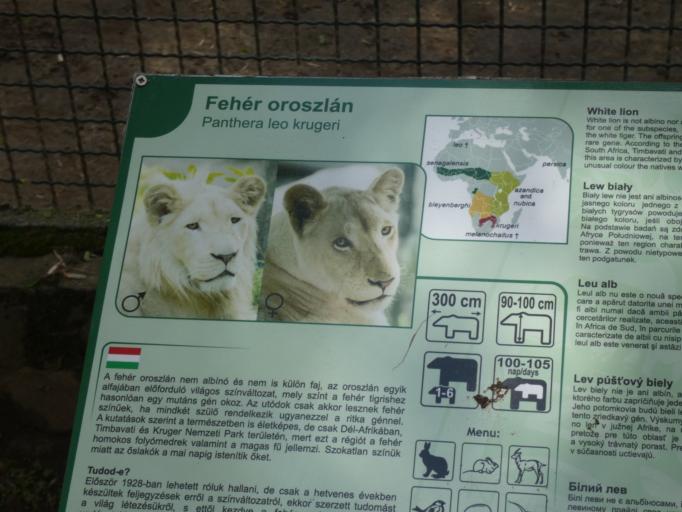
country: HU
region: Szabolcs-Szatmar-Bereg
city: Nyiregyhaza
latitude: 47.9988
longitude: 21.7269
